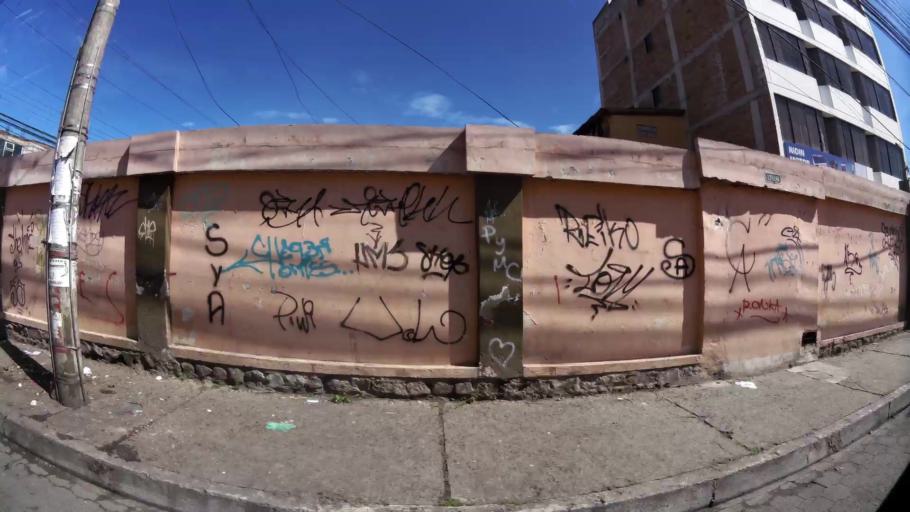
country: EC
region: Pichincha
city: Quito
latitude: -0.2771
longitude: -78.5553
